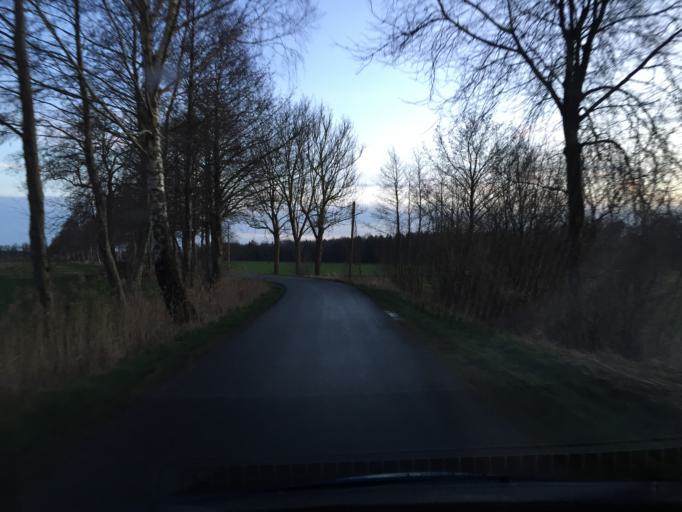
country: DE
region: Lower Saxony
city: Ludersburg
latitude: 53.3193
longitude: 10.6014
